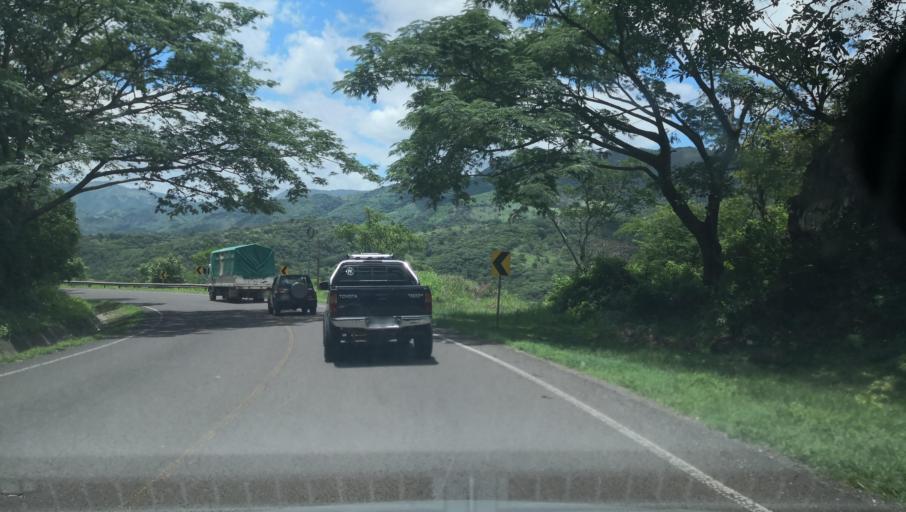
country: NI
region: Esteli
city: Condega
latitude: 13.2539
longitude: -86.3519
